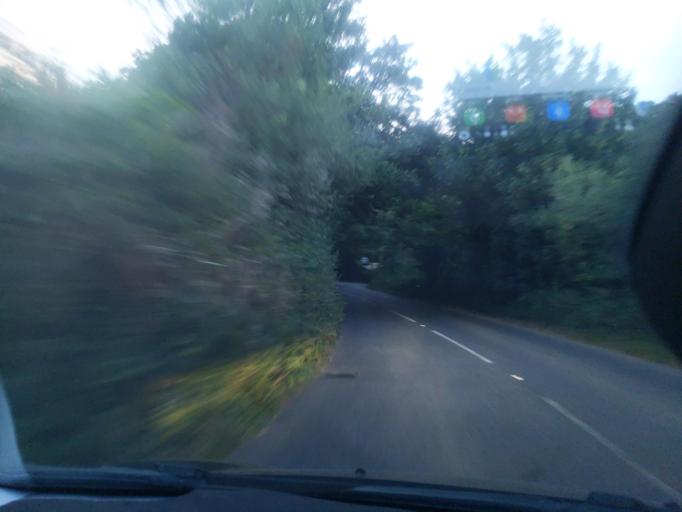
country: GB
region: England
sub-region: Cornwall
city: Camborne
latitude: 50.1911
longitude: -5.3067
